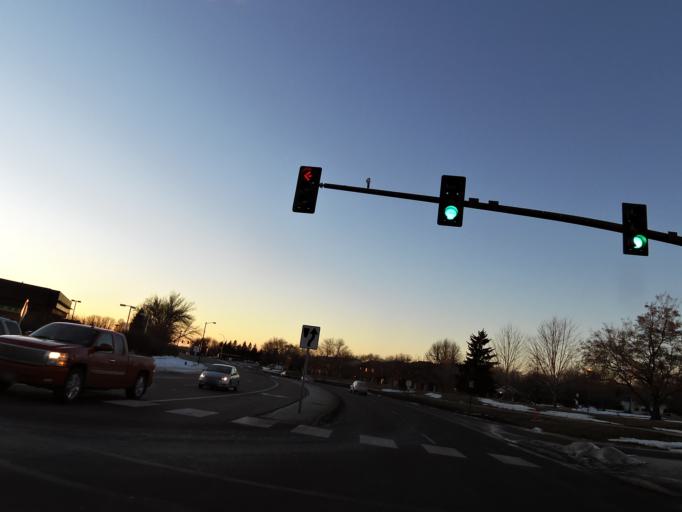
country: US
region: Minnesota
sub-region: Scott County
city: Savage
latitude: 44.8256
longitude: -93.3472
